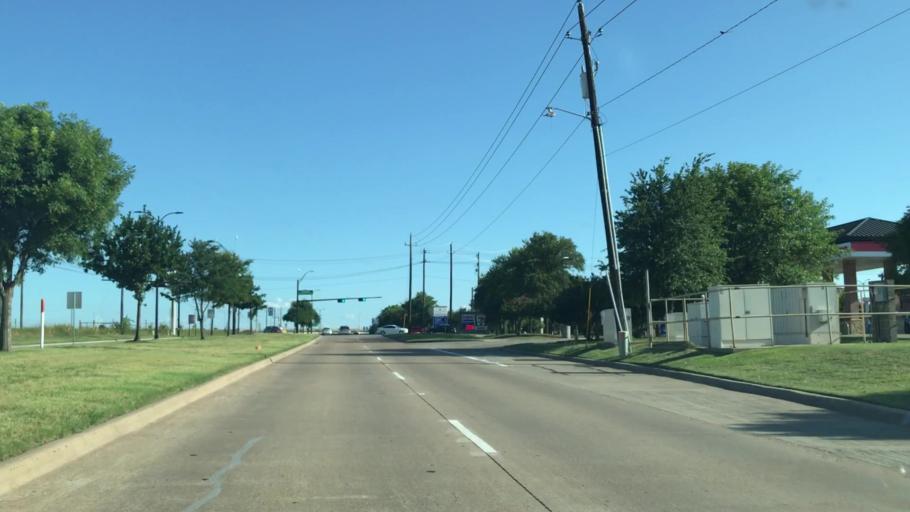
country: US
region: Texas
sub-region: Collin County
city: Frisco
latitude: 33.1171
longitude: -96.7681
